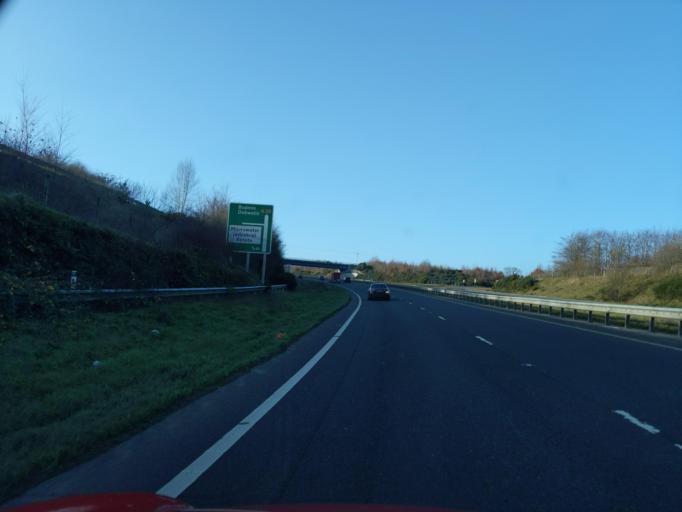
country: GB
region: England
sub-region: Cornwall
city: Liskeard
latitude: 50.4567
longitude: -4.4931
